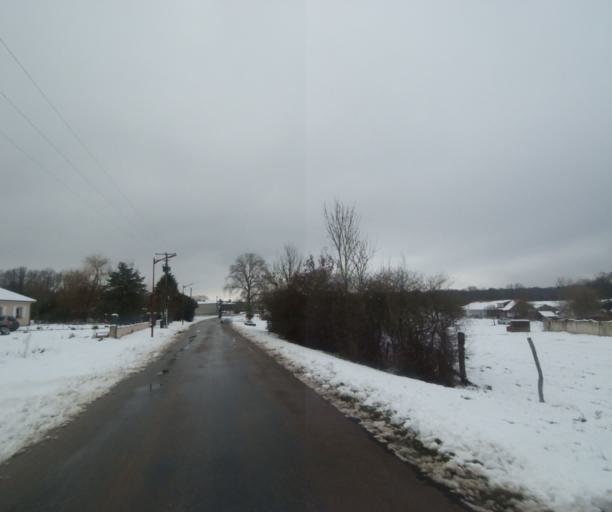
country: FR
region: Champagne-Ardenne
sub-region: Departement de la Haute-Marne
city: Laneuville-a-Remy
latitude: 48.4766
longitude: 4.8829
